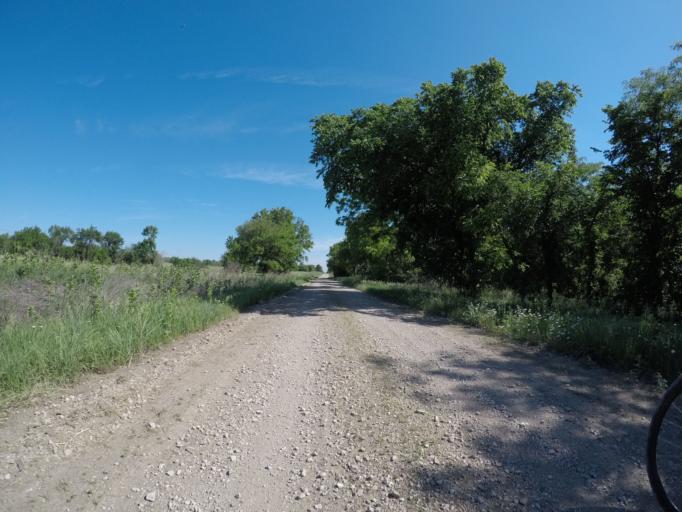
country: US
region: Kansas
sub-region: Wabaunsee County
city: Alma
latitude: 38.9386
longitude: -96.1138
